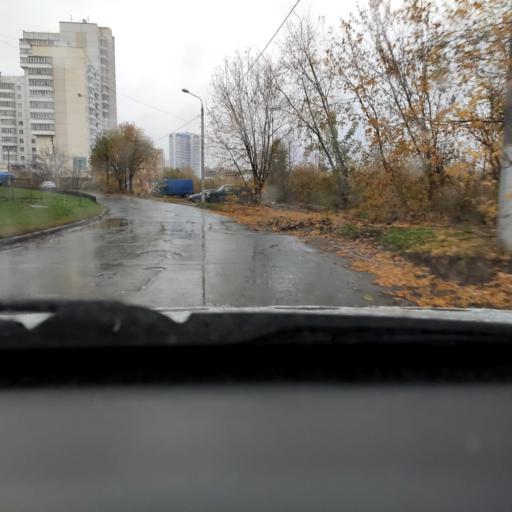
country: RU
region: Perm
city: Perm
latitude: 58.0125
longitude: 56.3109
